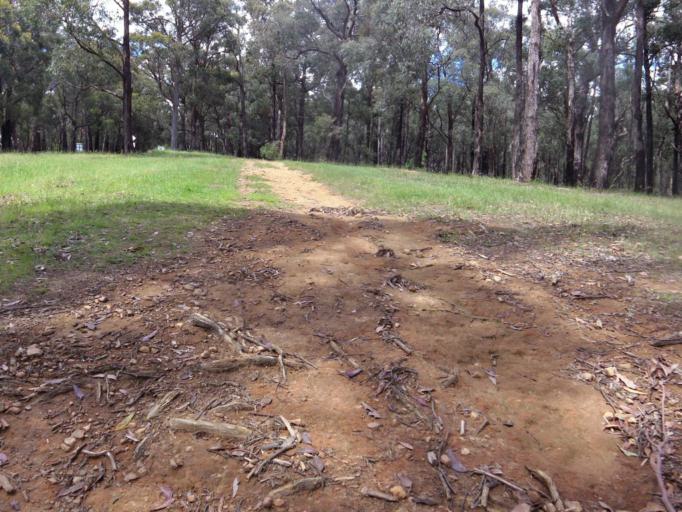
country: AU
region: Victoria
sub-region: Cardinia
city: Cockatoo
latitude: -37.9372
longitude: 145.4751
